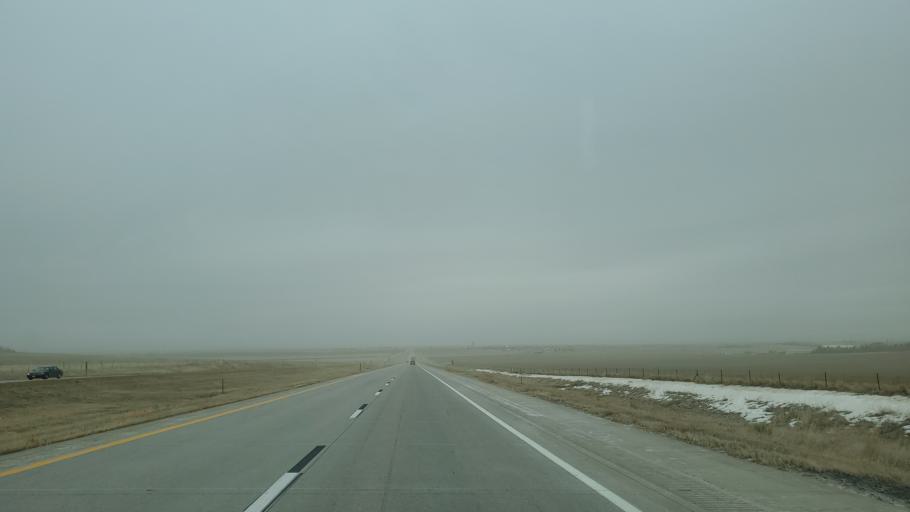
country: US
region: Colorado
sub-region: Adams County
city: Strasburg
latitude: 39.7287
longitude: -104.2748
